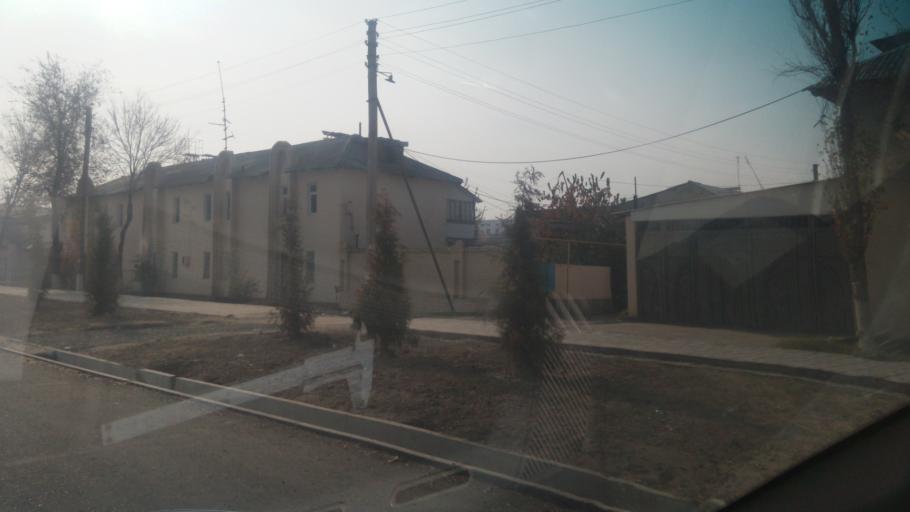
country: UZ
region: Sirdaryo
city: Guliston
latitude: 40.5085
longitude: 68.7733
